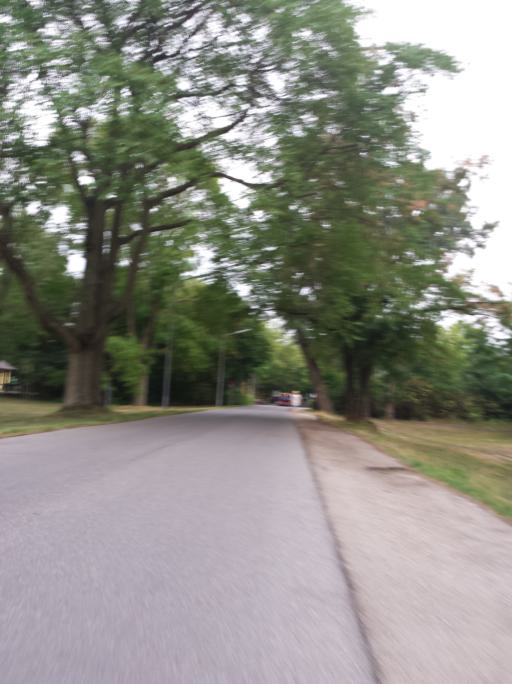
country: AT
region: Lower Austria
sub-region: Politischer Bezirk Wien-Umgebung
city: Schwechat
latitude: 48.1922
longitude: 16.4384
